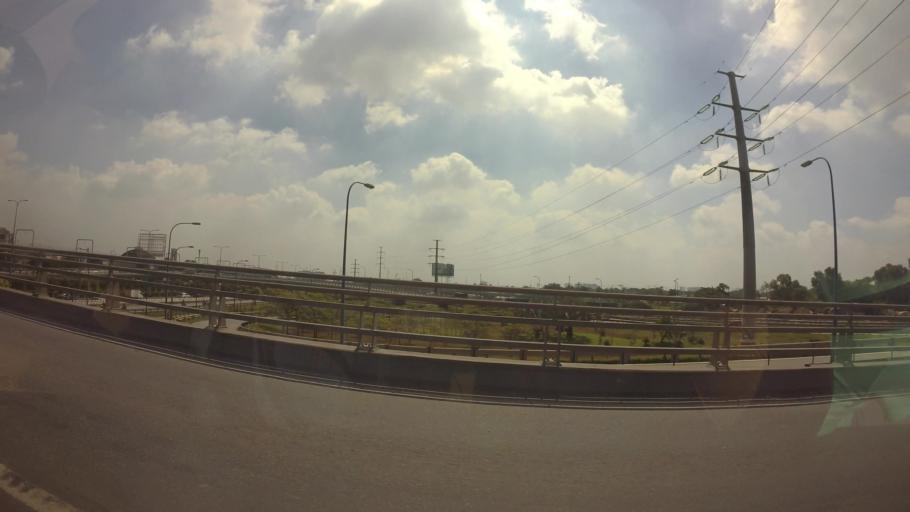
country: VN
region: Ho Chi Minh City
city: Quan Hai
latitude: 10.8018
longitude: 106.7534
